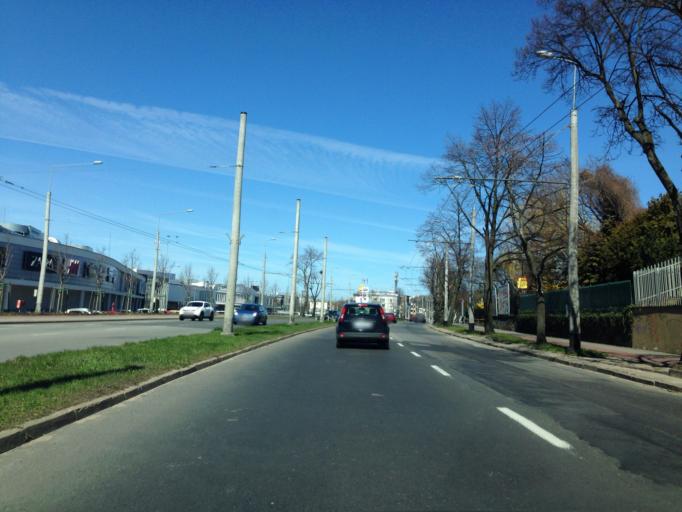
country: PL
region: Pomeranian Voivodeship
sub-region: Sopot
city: Sopot
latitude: 54.4734
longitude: 18.5540
